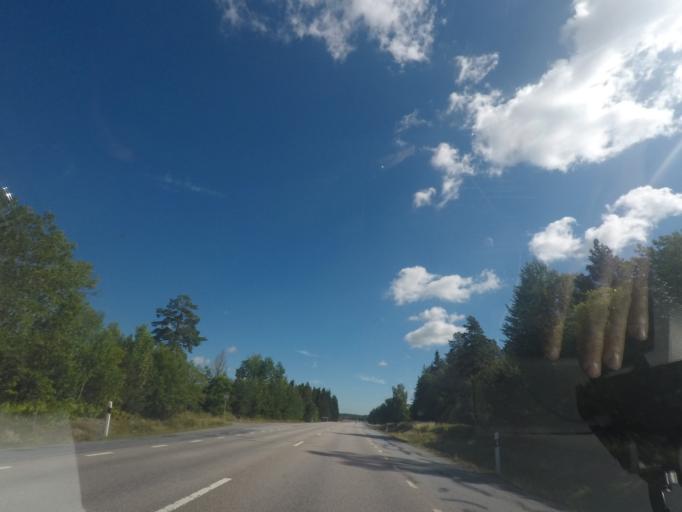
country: SE
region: Uppsala
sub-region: Enkopings Kommun
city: Orsundsbro
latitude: 59.7591
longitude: 17.3706
